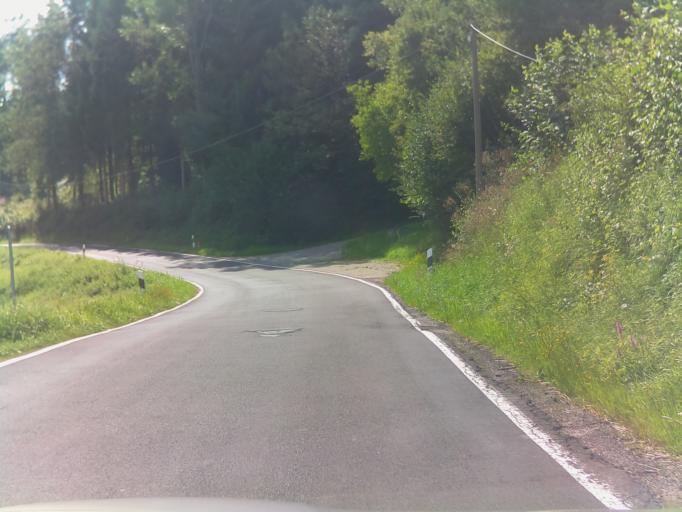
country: DE
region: Bavaria
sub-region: Regierungsbezirk Unterfranken
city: Kirchlauter
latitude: 50.0250
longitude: 10.7331
